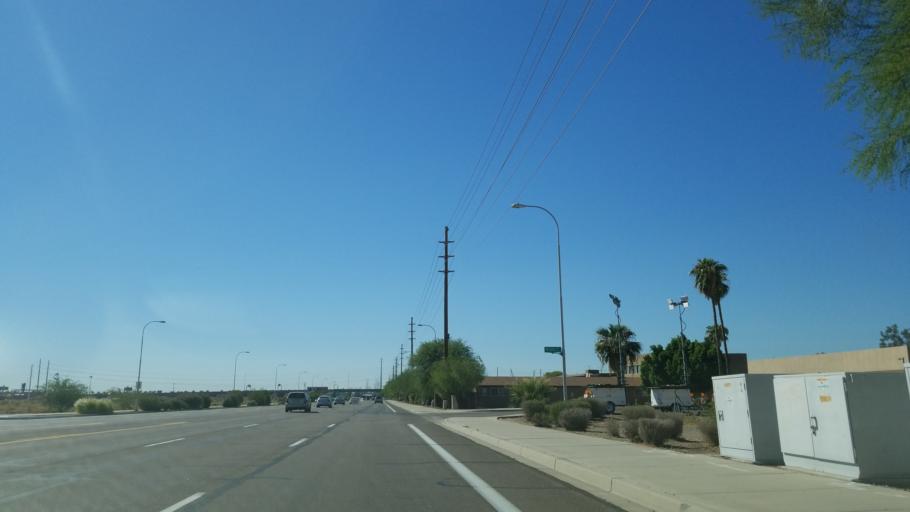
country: US
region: Arizona
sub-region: Maricopa County
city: Tempe
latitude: 33.4451
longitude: -111.9095
